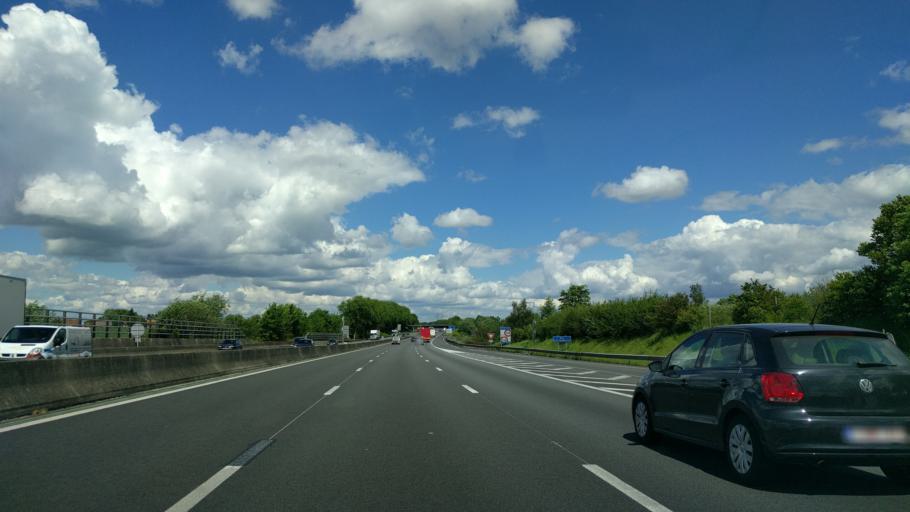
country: FR
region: Picardie
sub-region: Departement de la Somme
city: Chaulnes
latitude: 49.8906
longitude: 2.8406
